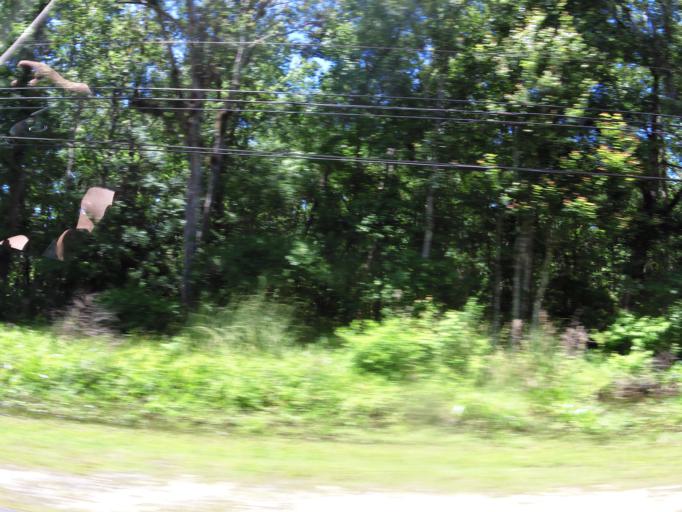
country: US
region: Florida
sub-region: Clay County
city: Green Cove Springs
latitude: 30.0160
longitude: -81.6046
